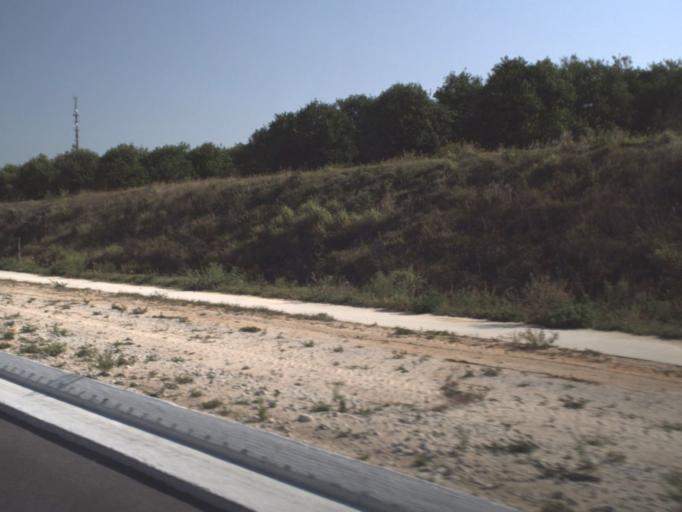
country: US
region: Florida
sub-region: Lake County
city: Clermont
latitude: 28.4600
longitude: -81.7203
